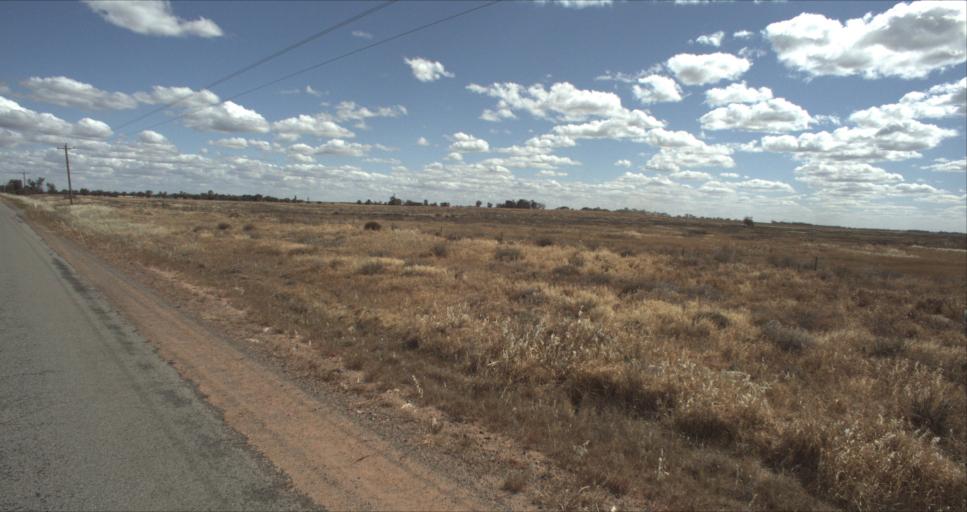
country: AU
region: New South Wales
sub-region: Leeton
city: Leeton
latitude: -34.4768
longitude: 146.2499
